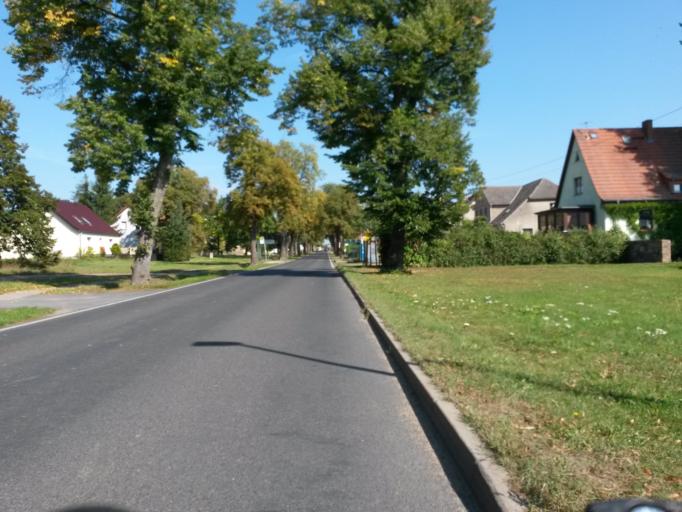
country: DE
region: Brandenburg
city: Templin
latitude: 53.0718
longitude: 13.4328
